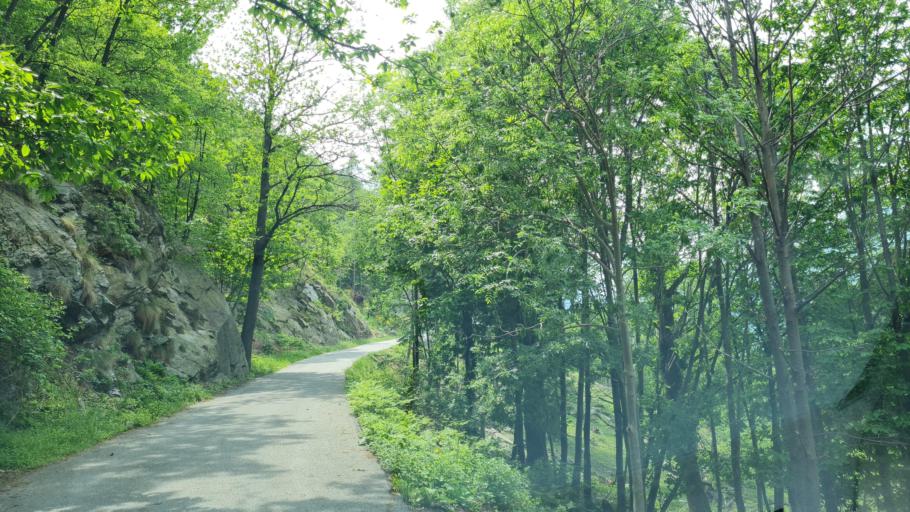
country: IT
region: Aosta Valley
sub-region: Valle d'Aosta
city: Bard
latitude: 45.6130
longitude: 7.7551
